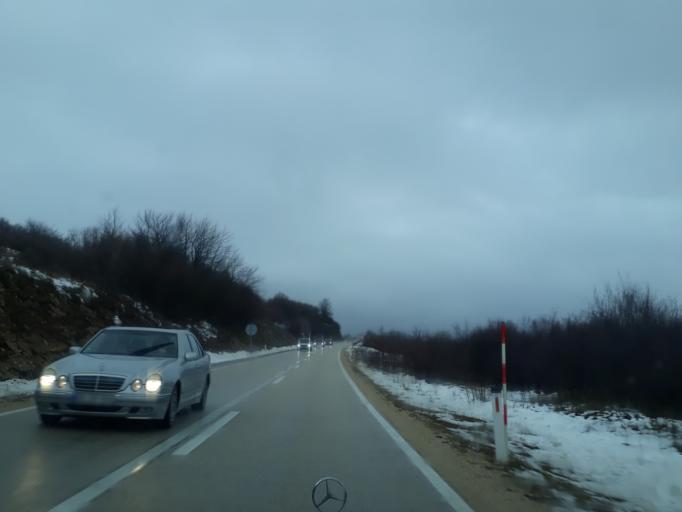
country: BA
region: Federation of Bosnia and Herzegovina
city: Tomislavgrad
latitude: 43.8050
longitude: 17.2046
